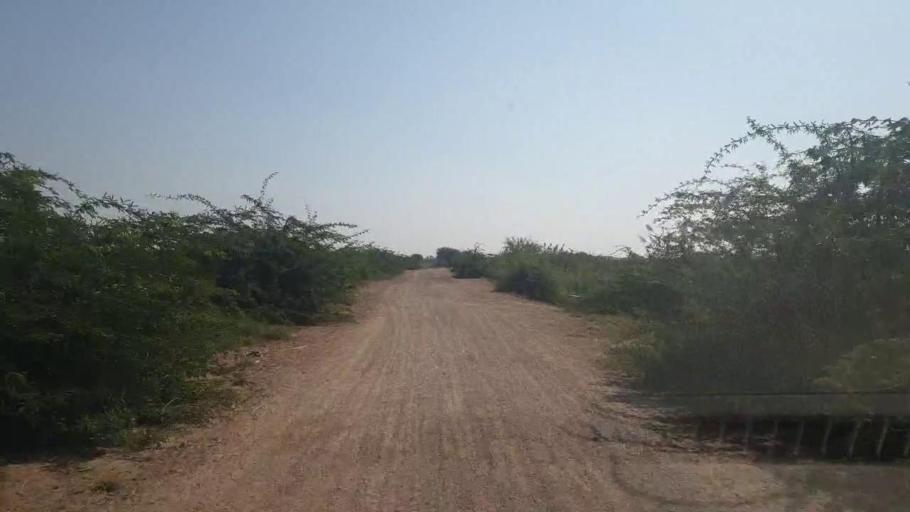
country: PK
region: Sindh
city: Badin
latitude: 24.5620
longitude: 68.8459
